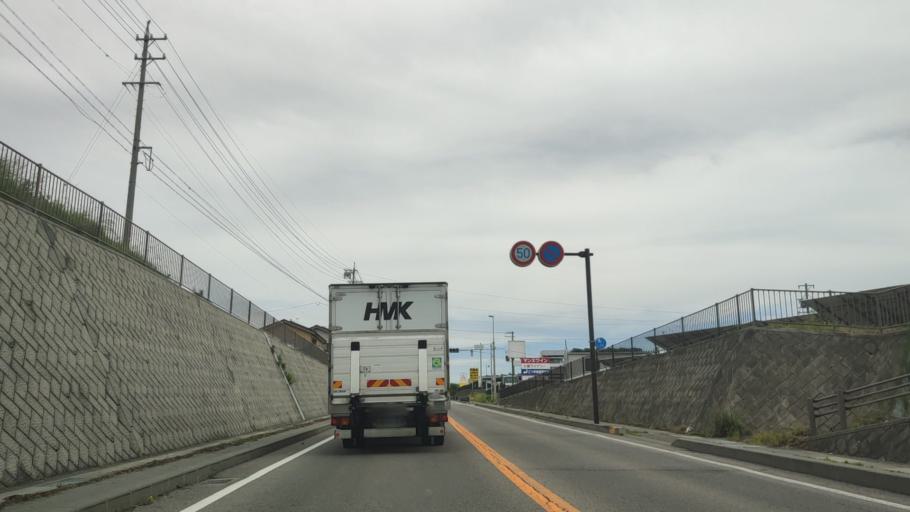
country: JP
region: Nagano
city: Komoro
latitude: 36.3353
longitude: 138.4230
